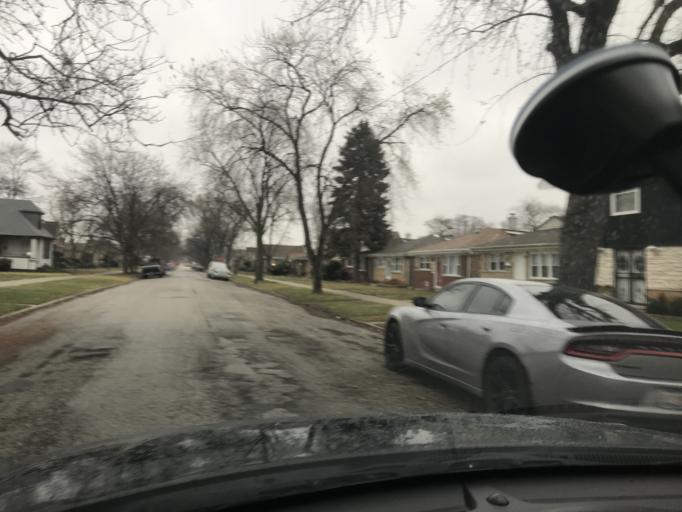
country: US
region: Illinois
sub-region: Cook County
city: Calumet Park
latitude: 41.7187
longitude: -87.6382
